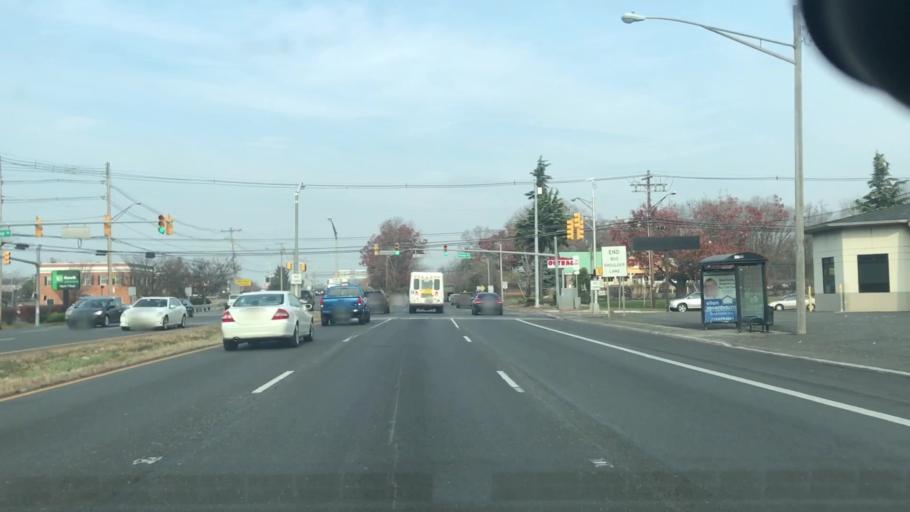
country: US
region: New Jersey
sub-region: Middlesex County
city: Madison Park
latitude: 40.4349
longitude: -74.3015
